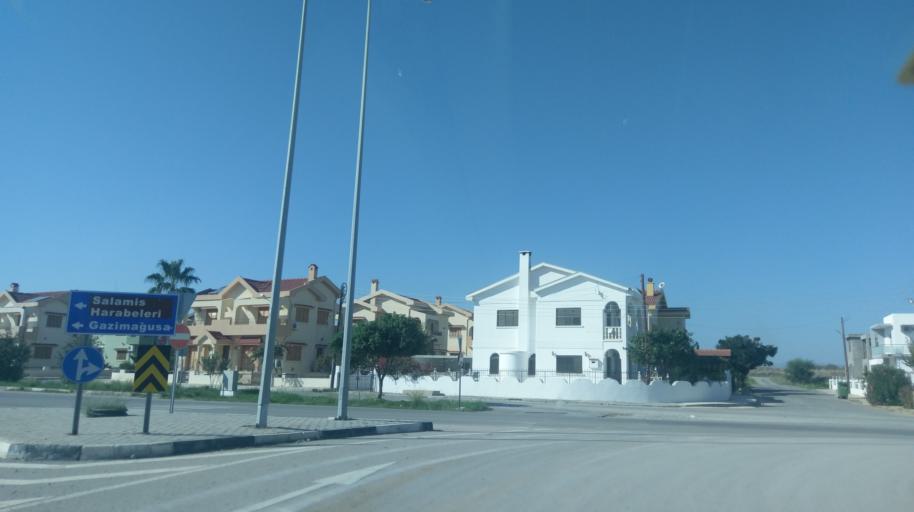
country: CY
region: Ammochostos
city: Trikomo
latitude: 35.2683
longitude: 33.9145
